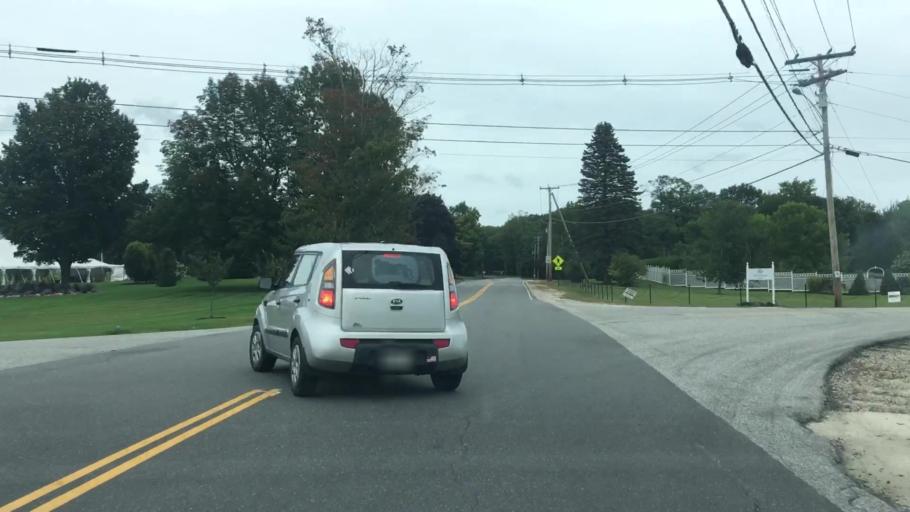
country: US
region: Maine
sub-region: Cumberland County
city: New Gloucester
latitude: 43.8998
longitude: -70.2561
